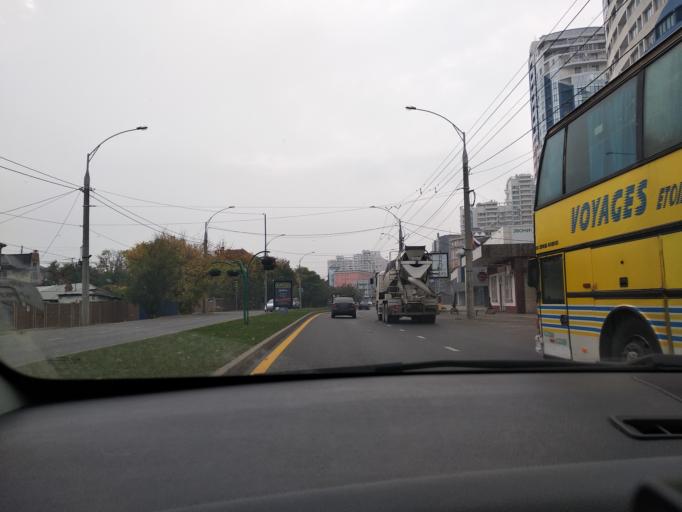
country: RU
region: Krasnodarskiy
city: Krasnodar
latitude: 45.0278
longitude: 38.9597
